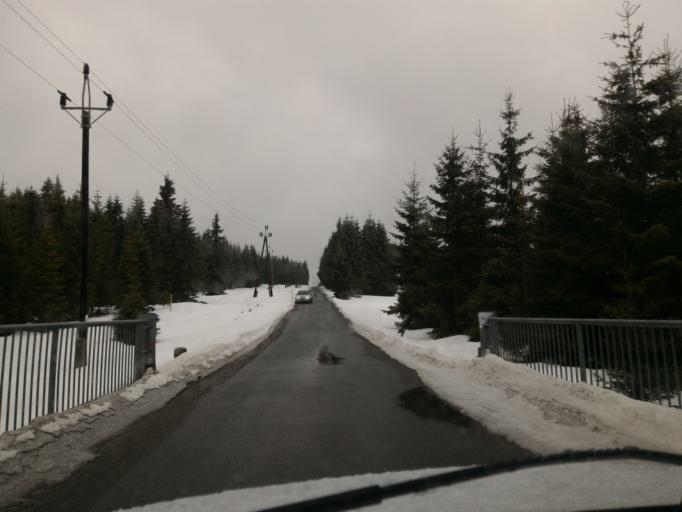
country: CZ
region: Liberecky
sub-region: Okres Jablonec nad Nisou
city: Korenov
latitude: 50.8001
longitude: 15.3530
